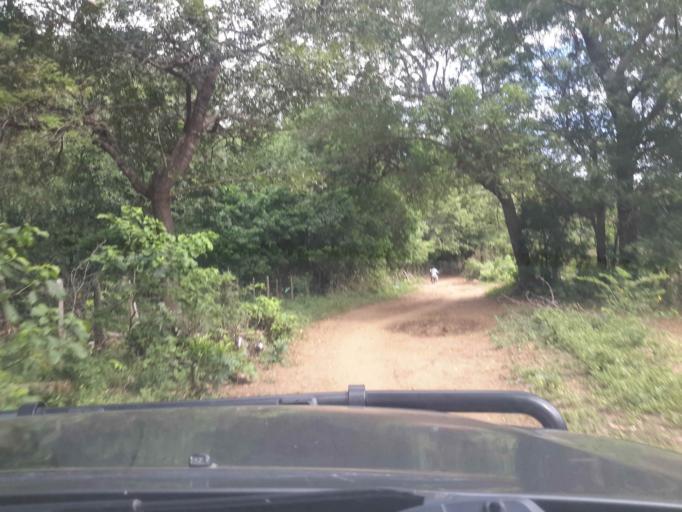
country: NI
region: Carazo
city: Santa Teresa
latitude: 11.6767
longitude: -86.3027
